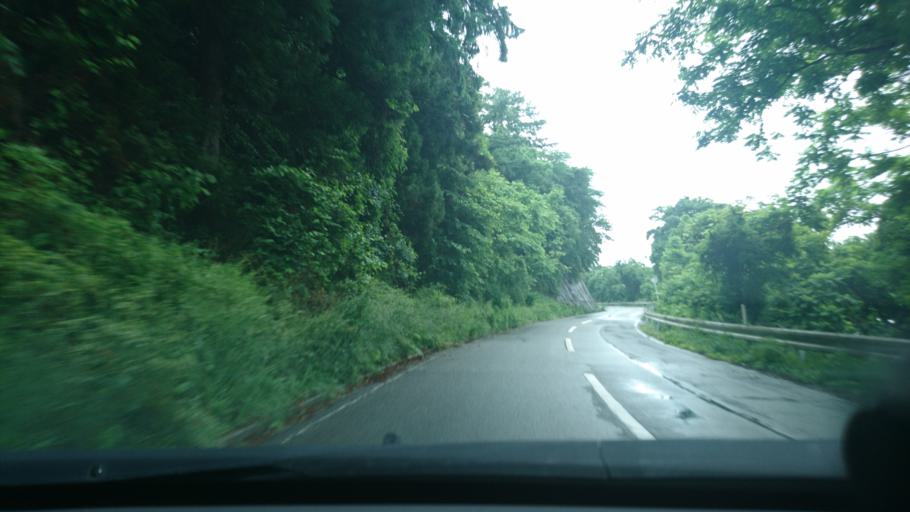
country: JP
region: Miyagi
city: Wakuya
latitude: 38.6829
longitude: 141.2843
